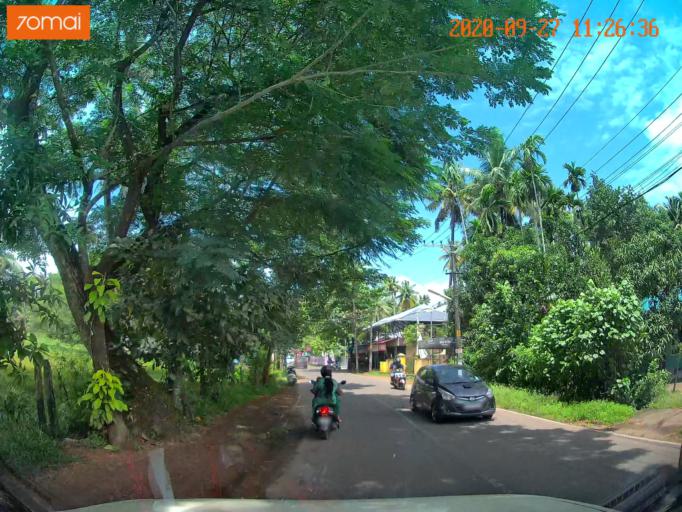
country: IN
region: Kerala
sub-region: Thrissur District
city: Thanniyam
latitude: 10.4165
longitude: 76.1539
